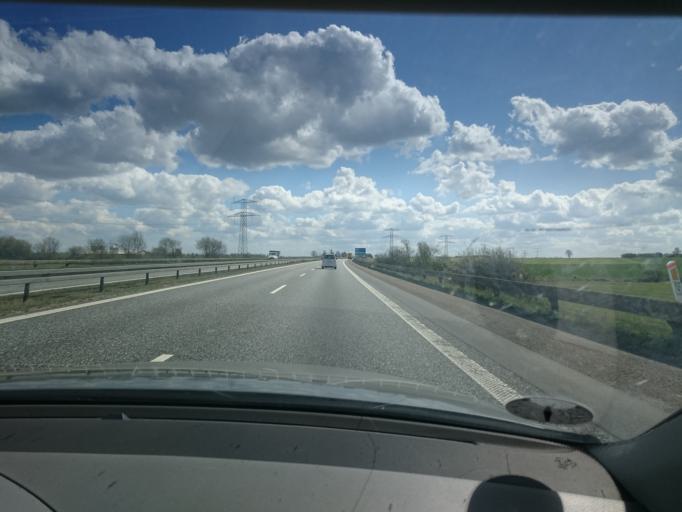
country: DK
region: Central Jutland
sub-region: Randers Kommune
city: Spentrup
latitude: 56.5071
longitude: 9.9730
